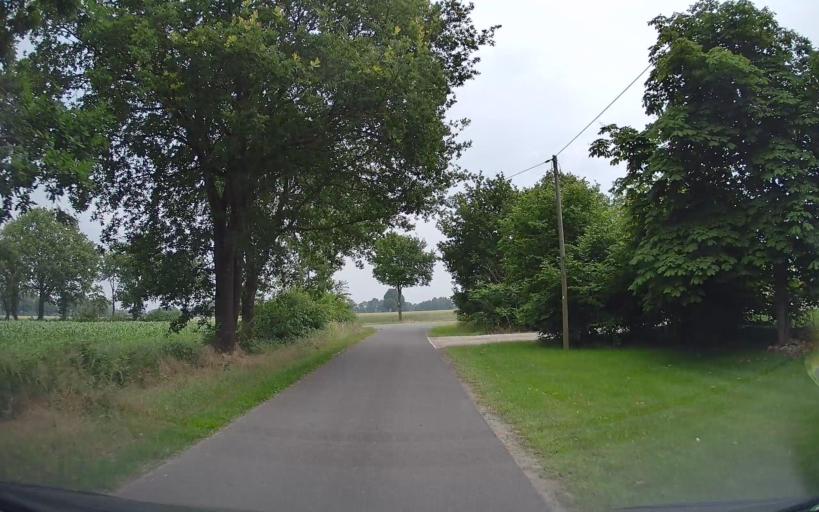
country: DE
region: Lower Saxony
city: Friesoythe
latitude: 53.0562
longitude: 7.8632
